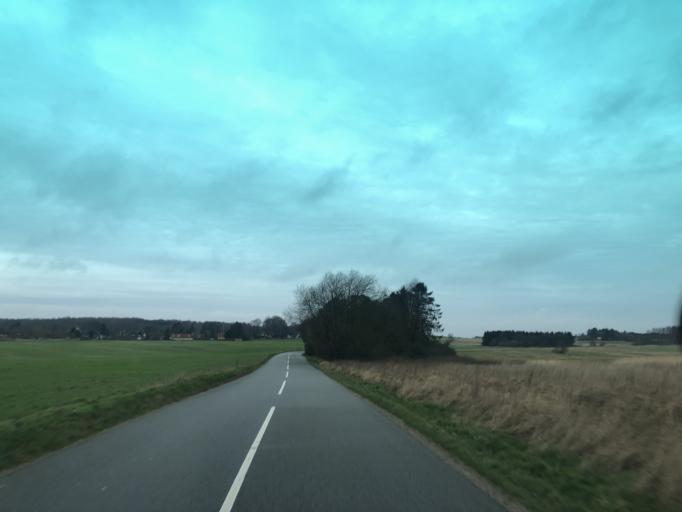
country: DK
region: Capital Region
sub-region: Frederikssund Kommune
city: Slangerup
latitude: 55.8594
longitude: 12.2312
